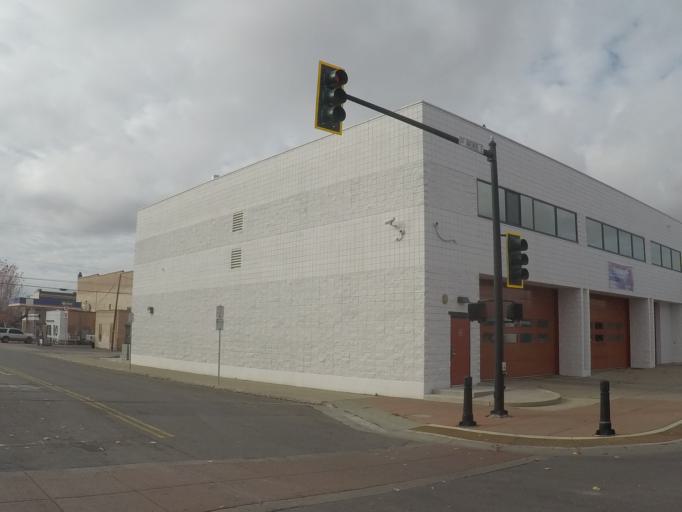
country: US
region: Montana
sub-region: Flathead County
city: Kalispell
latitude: 48.1951
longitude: -114.3109
